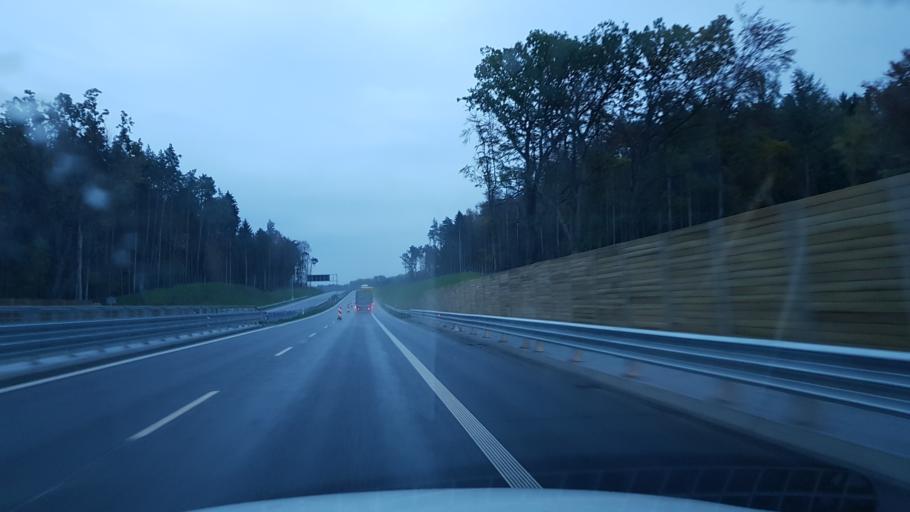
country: PL
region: West Pomeranian Voivodeship
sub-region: Powiat gryficki
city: Ploty
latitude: 53.8269
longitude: 15.2769
